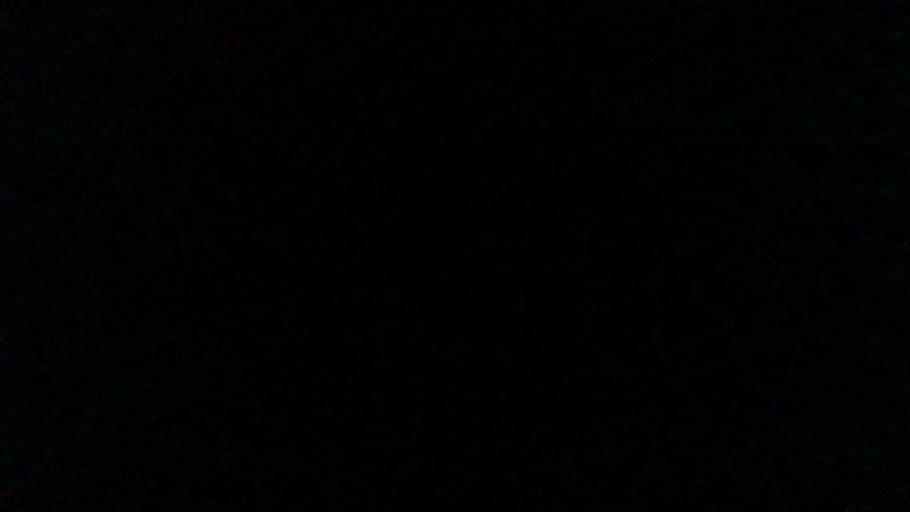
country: US
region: Tennessee
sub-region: Coffee County
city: New Union
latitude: 35.5547
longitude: -86.1979
